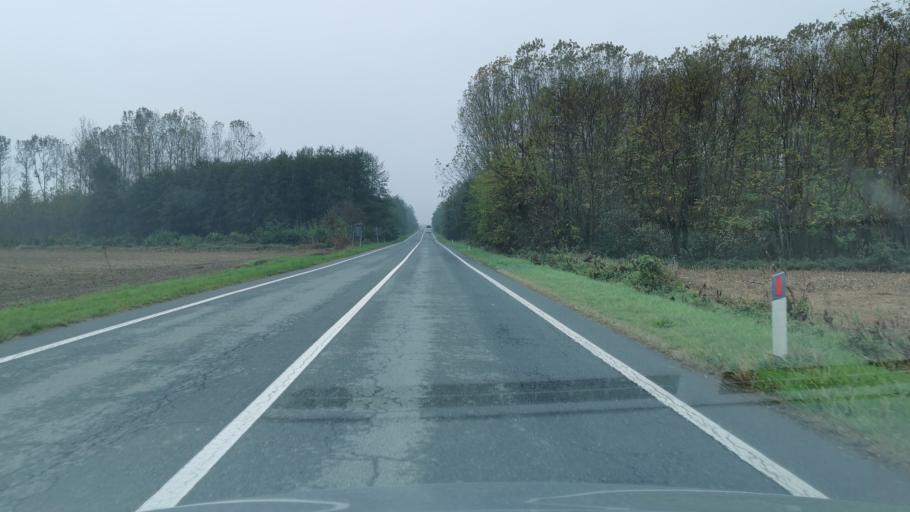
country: IT
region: Piedmont
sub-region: Provincia di Torino
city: Strambino
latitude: 45.3862
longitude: 7.9017
